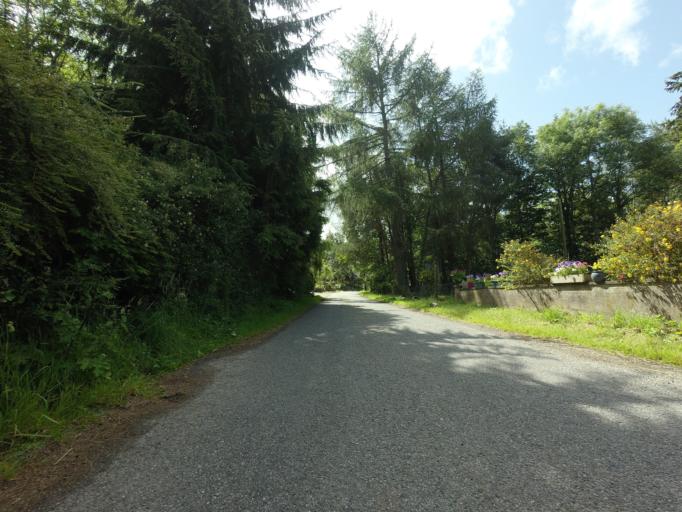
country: GB
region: Scotland
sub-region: Highland
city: Nairn
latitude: 57.4976
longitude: -3.9990
